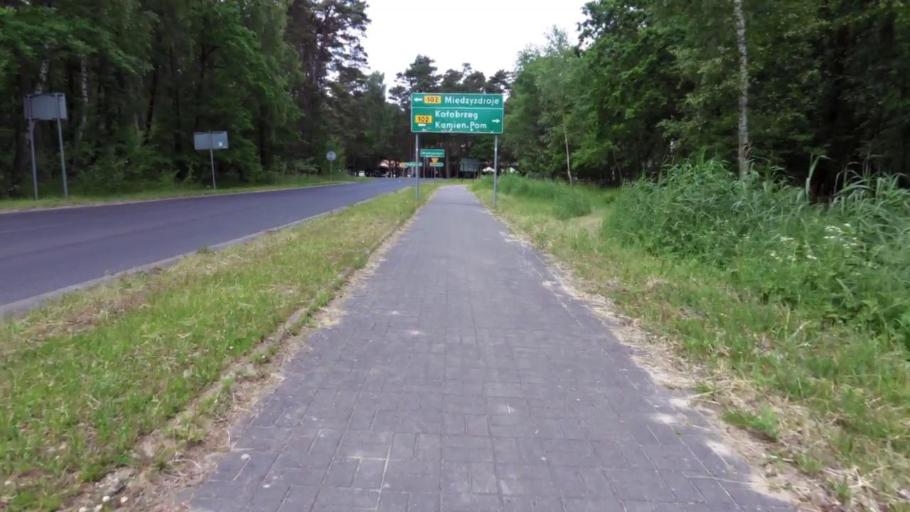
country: PL
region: West Pomeranian Voivodeship
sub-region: Powiat kamienski
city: Dziwnow
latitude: 53.9995
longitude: 14.6774
